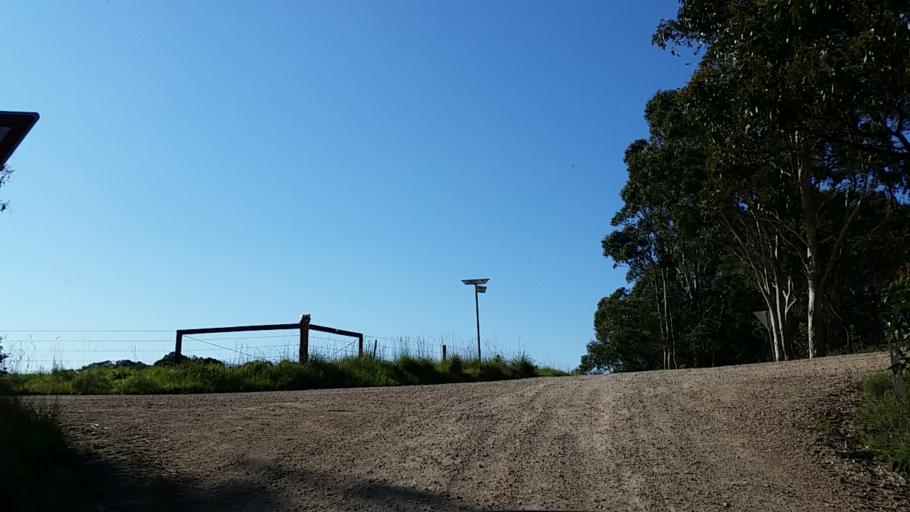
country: AU
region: South Australia
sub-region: Adelaide Hills
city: Lobethal
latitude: -34.8873
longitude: 138.8548
